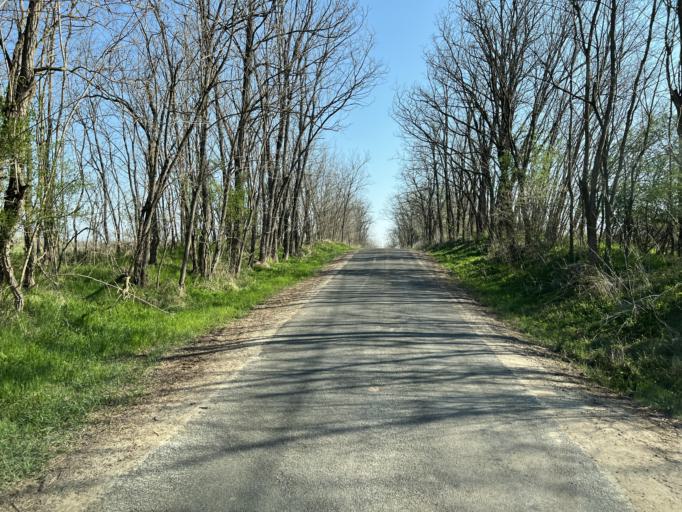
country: SK
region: Nitriansky
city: Sahy
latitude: 48.0287
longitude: 18.8310
